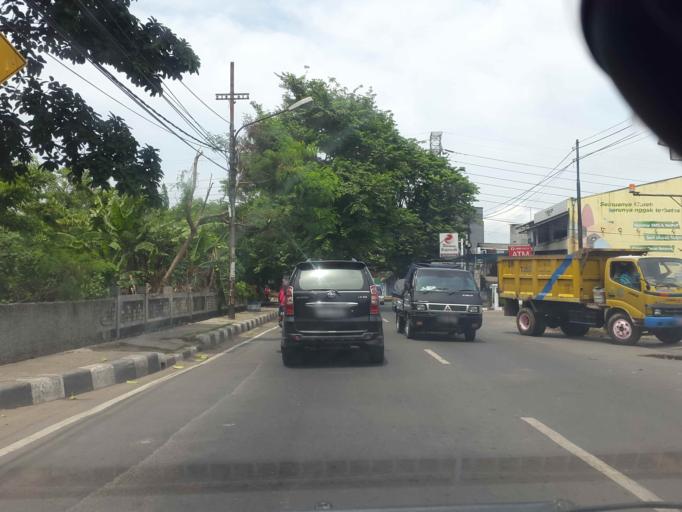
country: ID
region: Banten
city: Tangerang
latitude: -6.1612
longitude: 106.6328
